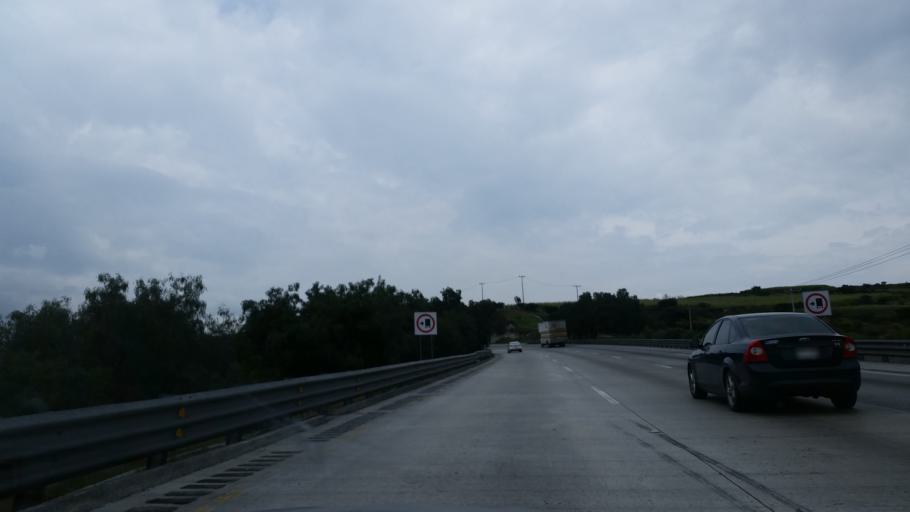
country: MX
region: Hidalgo
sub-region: Tepeji del Rio de Ocampo
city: Cantera de Villagran
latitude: 19.8599
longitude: -99.3146
